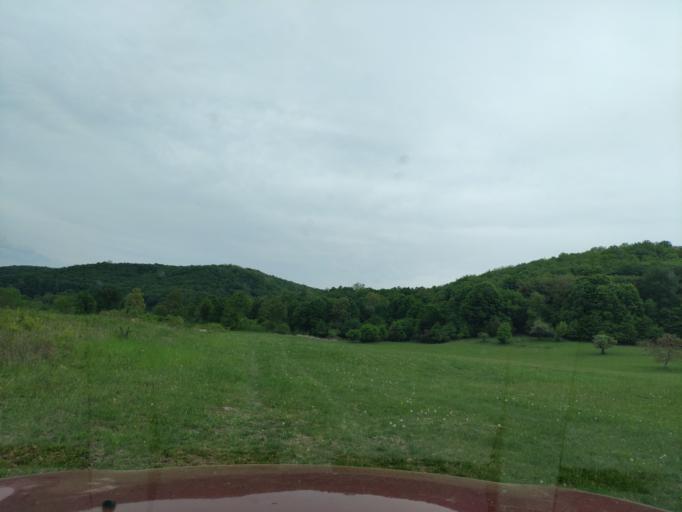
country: SK
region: Banskobystricky
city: Revuca
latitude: 48.5175
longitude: 20.1322
